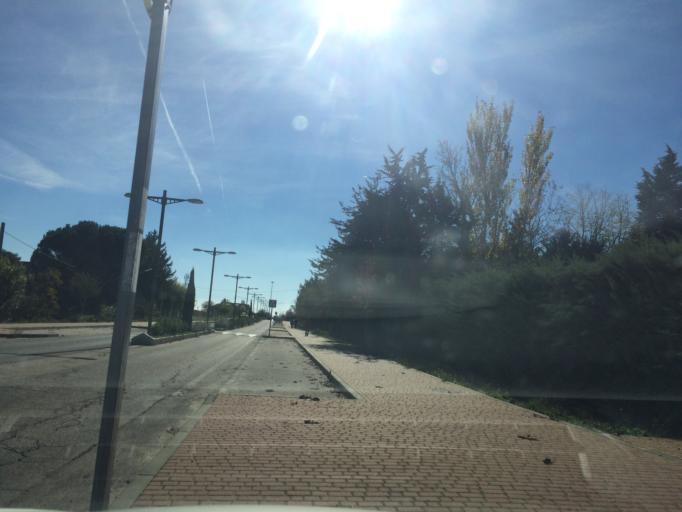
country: ES
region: Madrid
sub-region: Provincia de Madrid
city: La Cabrera
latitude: 40.8604
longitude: -3.6135
